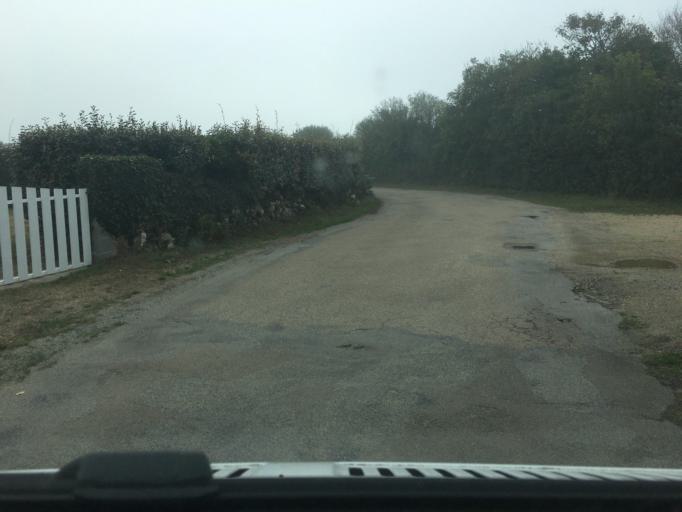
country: FR
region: Brittany
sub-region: Departement du Finistere
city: Plogoff
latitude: 48.0321
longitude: -4.6971
